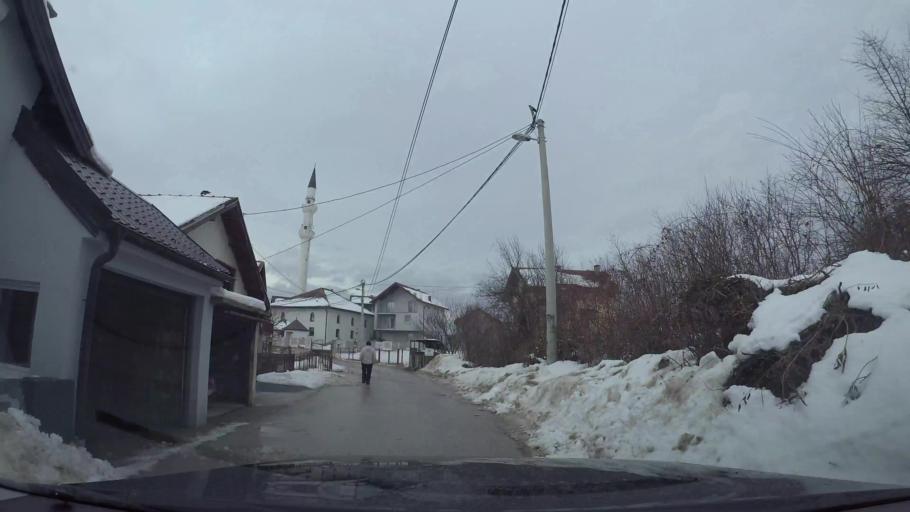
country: BA
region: Federation of Bosnia and Herzegovina
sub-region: Kanton Sarajevo
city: Sarajevo
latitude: 43.8648
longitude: 18.3321
